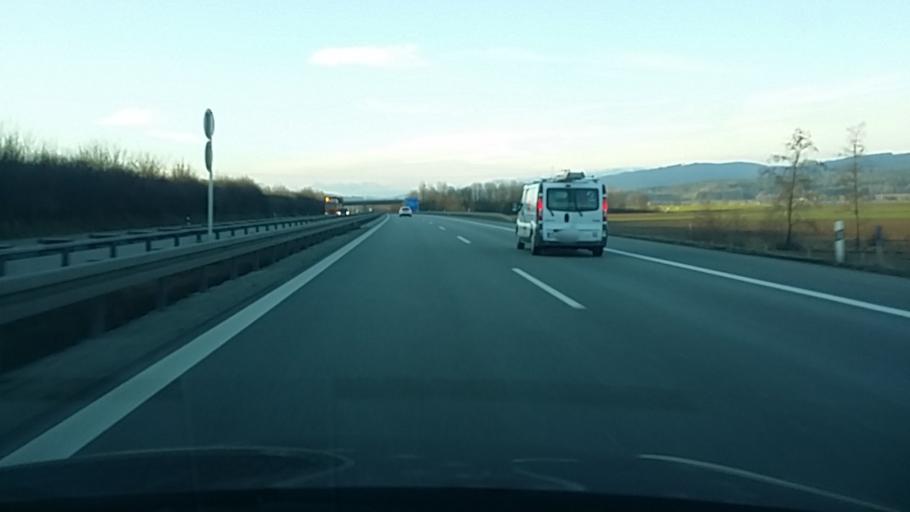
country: DE
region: Bavaria
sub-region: Lower Bavaria
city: Kirchroth
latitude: 48.9527
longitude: 12.5562
